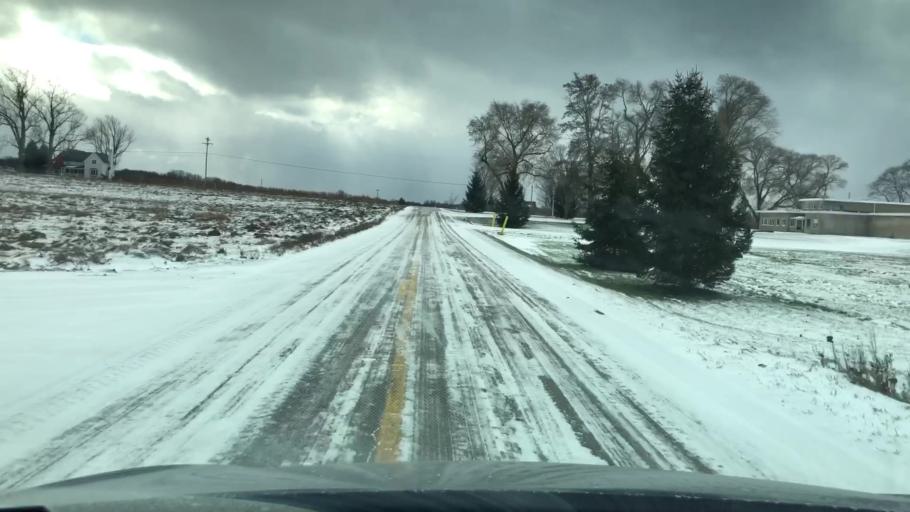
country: US
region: Michigan
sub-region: Antrim County
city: Elk Rapids
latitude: 44.9227
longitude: -85.5156
